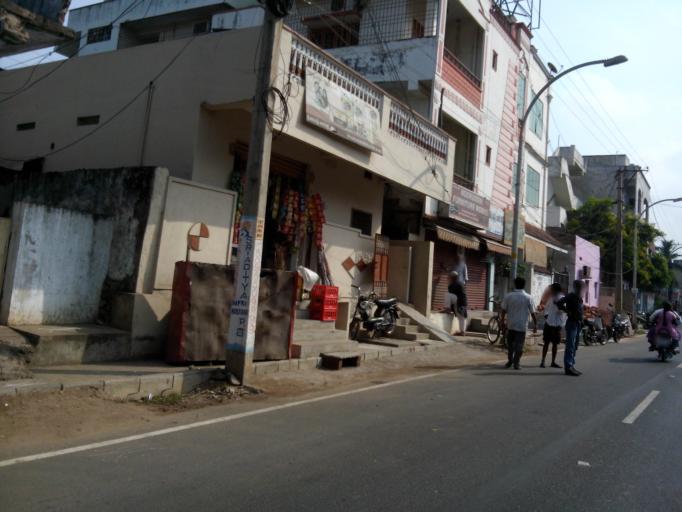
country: IN
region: Andhra Pradesh
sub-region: Krishna
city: Vijayawada
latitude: 16.5232
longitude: 80.6674
